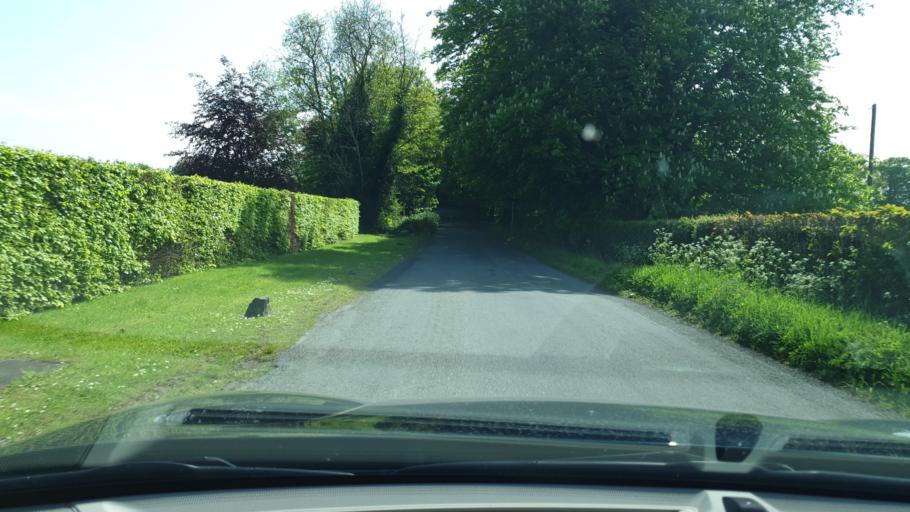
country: IE
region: Leinster
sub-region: An Mhi
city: Dunshaughlin
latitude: 53.4777
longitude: -6.5387
